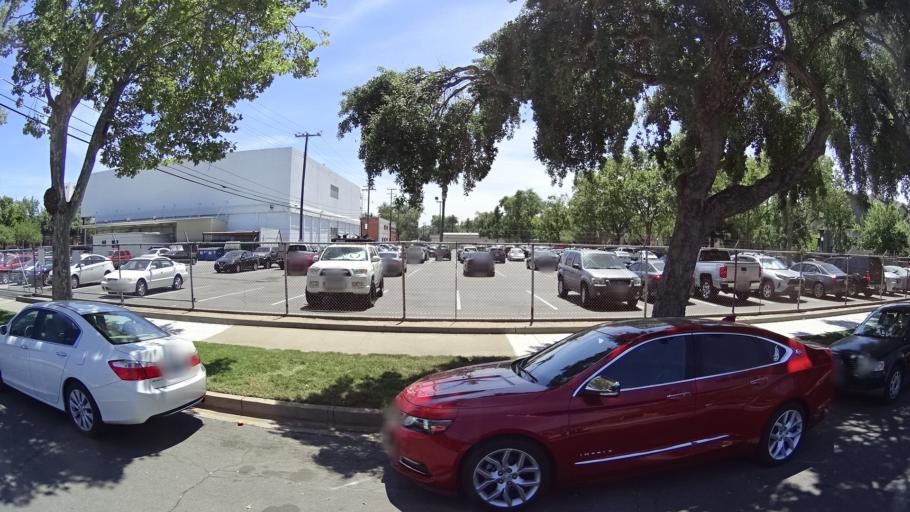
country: US
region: California
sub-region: Sacramento County
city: Sacramento
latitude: 38.5847
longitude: -121.4809
